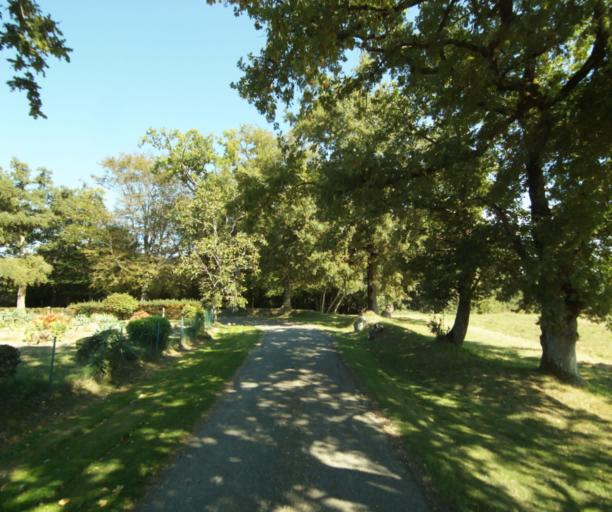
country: FR
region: Midi-Pyrenees
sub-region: Departement du Gers
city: Cazaubon
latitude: 43.9447
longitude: -0.0215
